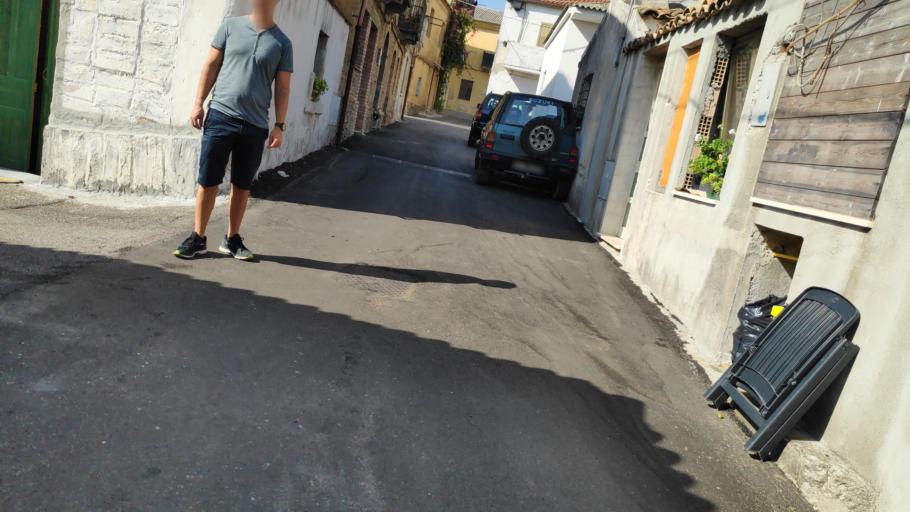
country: IT
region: Calabria
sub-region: Provincia di Catanzaro
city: Caraffa di Catanzaro
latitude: 38.8821
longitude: 16.4865
